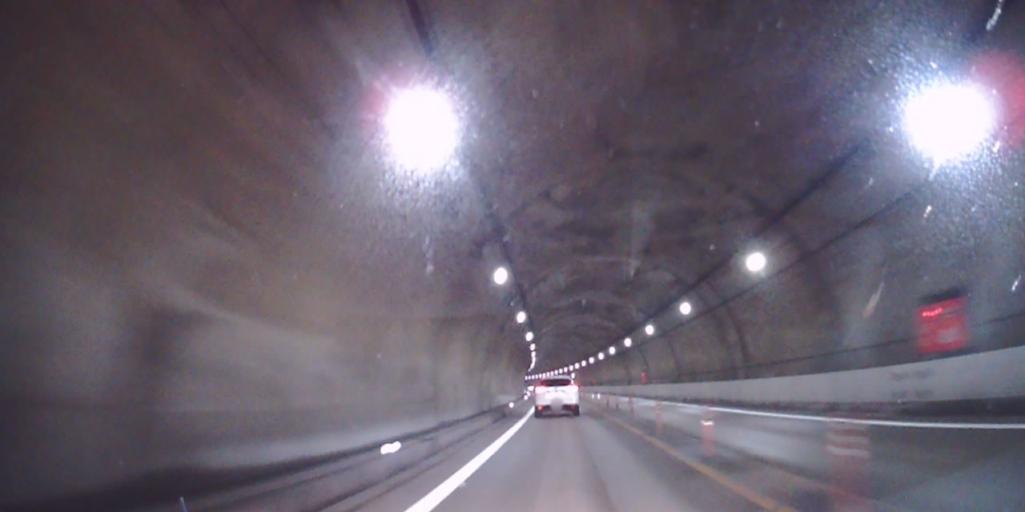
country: JP
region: Hokkaido
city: Date
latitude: 42.5881
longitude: 140.7231
